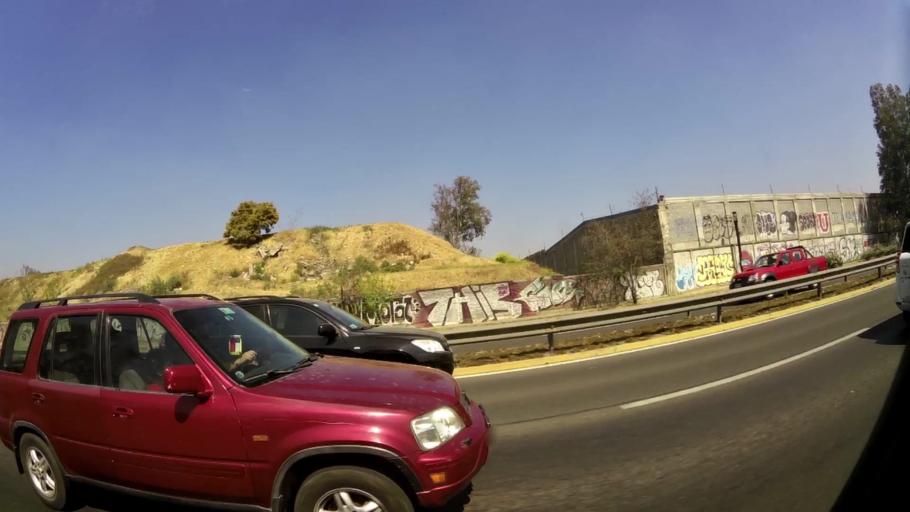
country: CL
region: Santiago Metropolitan
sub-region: Provincia de Santiago
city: Santiago
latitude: -33.4769
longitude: -70.6779
